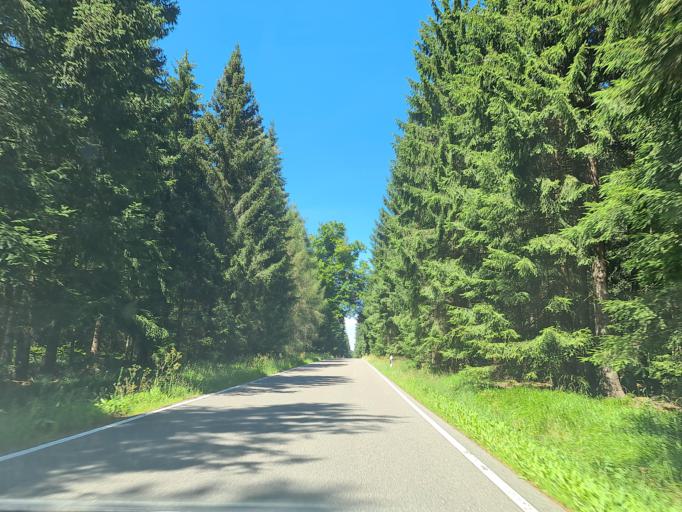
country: DE
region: Saxony
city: Rechenberg-Bienenmuhle
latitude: 50.7166
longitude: 13.5315
